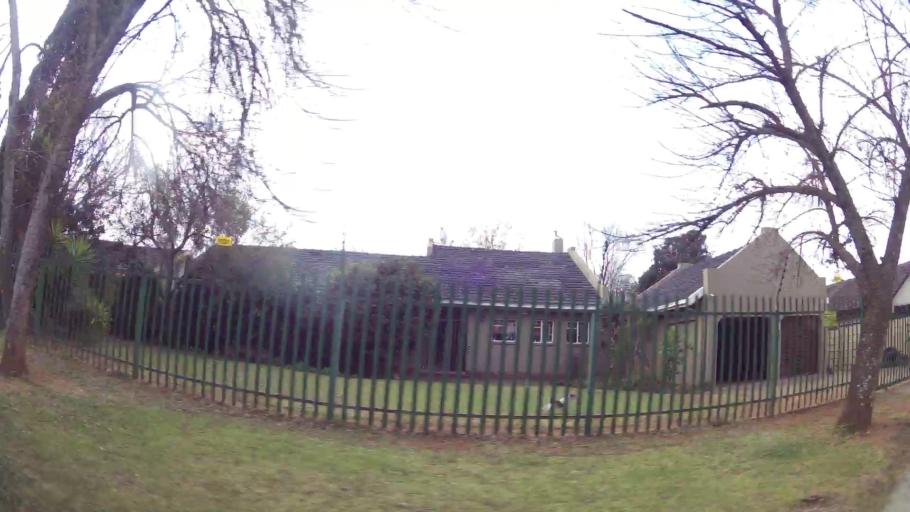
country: ZA
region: Mpumalanga
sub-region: Nkangala District Municipality
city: Delmas
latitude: -26.1408
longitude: 28.6697
